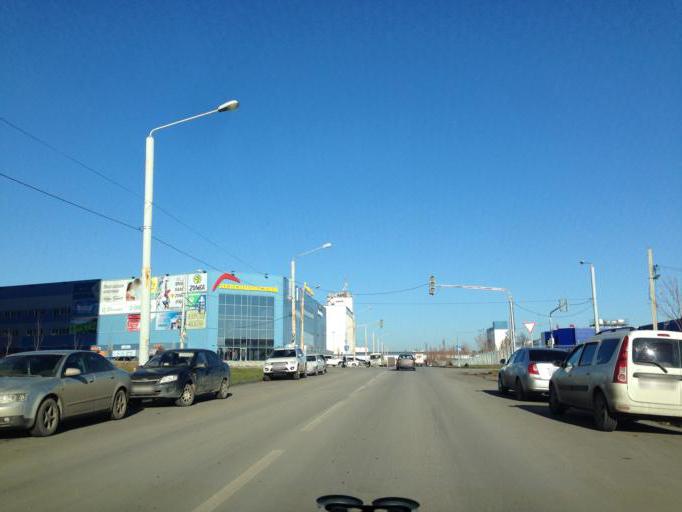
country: RU
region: Rostov
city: Kalinin
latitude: 47.2346
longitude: 39.6053
